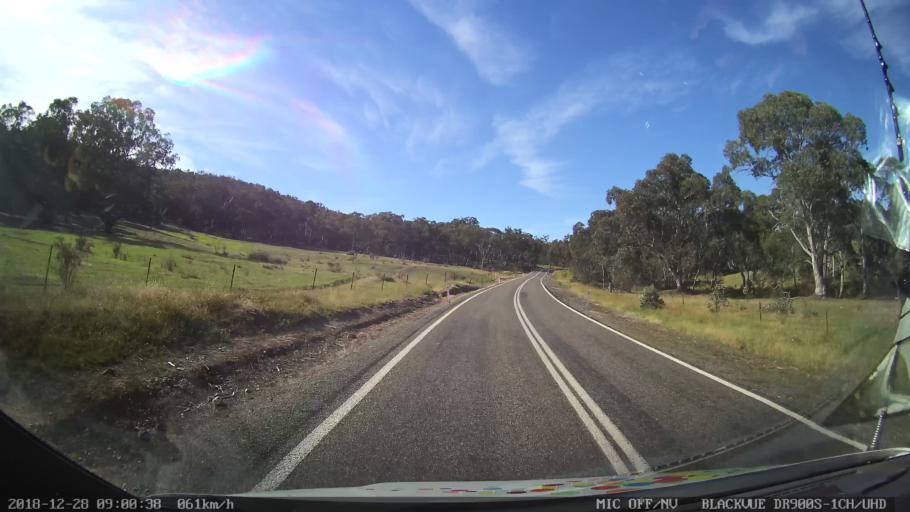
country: AU
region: New South Wales
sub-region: Upper Lachlan Shire
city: Crookwell
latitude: -34.1401
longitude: 149.3348
